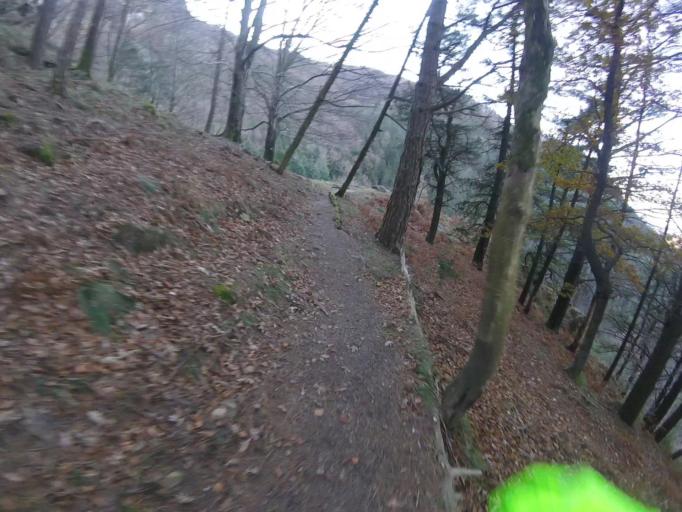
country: ES
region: Basque Country
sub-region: Provincia de Guipuzcoa
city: Irun
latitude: 43.2860
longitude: -1.7915
